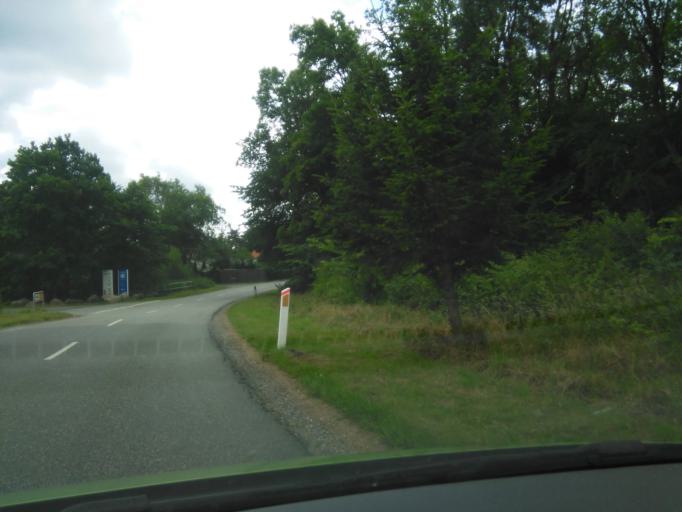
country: DK
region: Central Jutland
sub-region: Arhus Kommune
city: Logten
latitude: 56.2461
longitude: 10.3341
